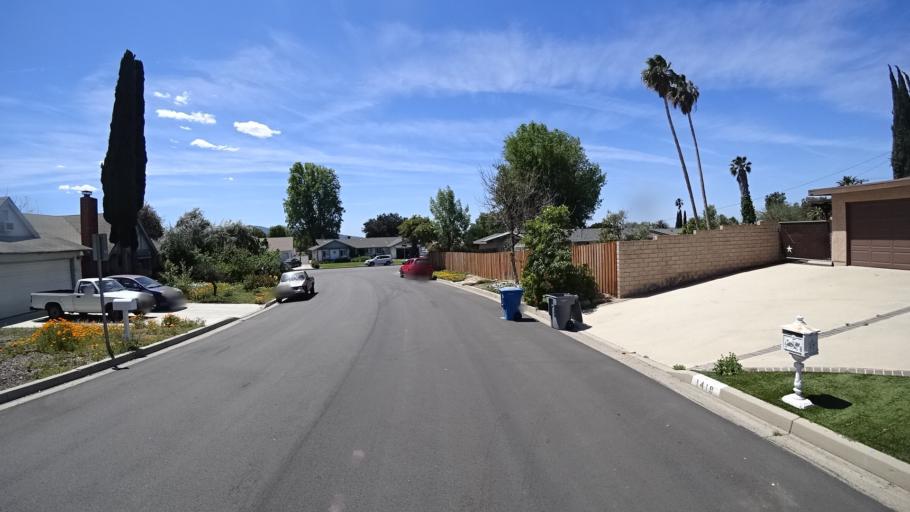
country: US
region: California
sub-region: Ventura County
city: Thousand Oaks
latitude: 34.2168
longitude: -118.8531
